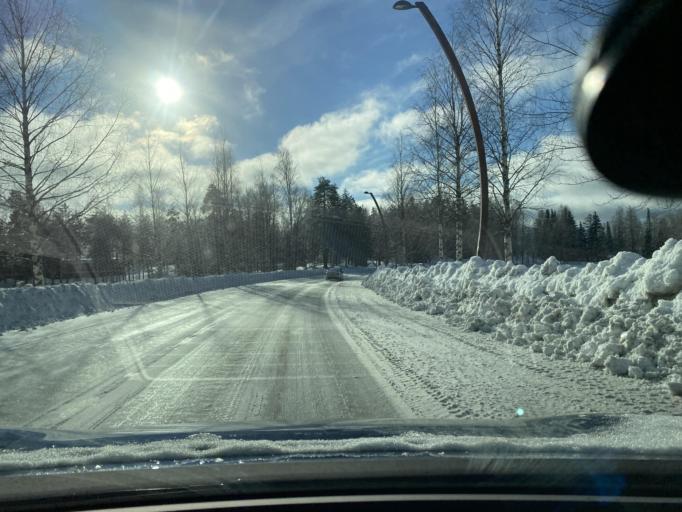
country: FI
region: Southern Savonia
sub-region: Mikkeli
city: Kangasniemi
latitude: 61.9953
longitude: 26.6478
